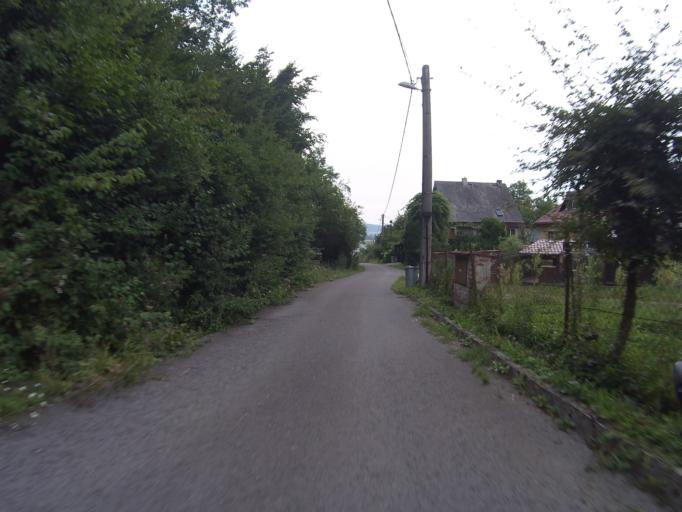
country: SK
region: Nitriansky
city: Ilava
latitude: 49.0354
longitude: 18.3126
